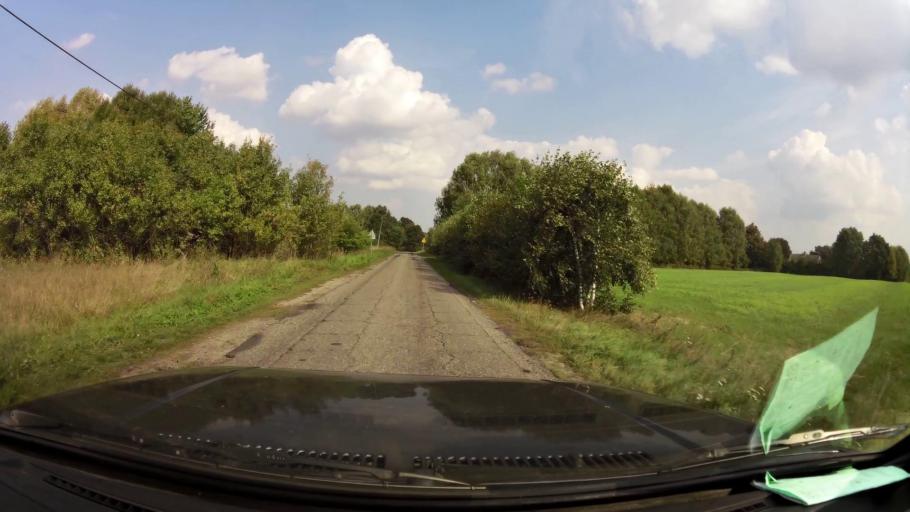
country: PL
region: West Pomeranian Voivodeship
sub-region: Powiat koszalinski
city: Polanow
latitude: 54.1248
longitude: 16.5173
